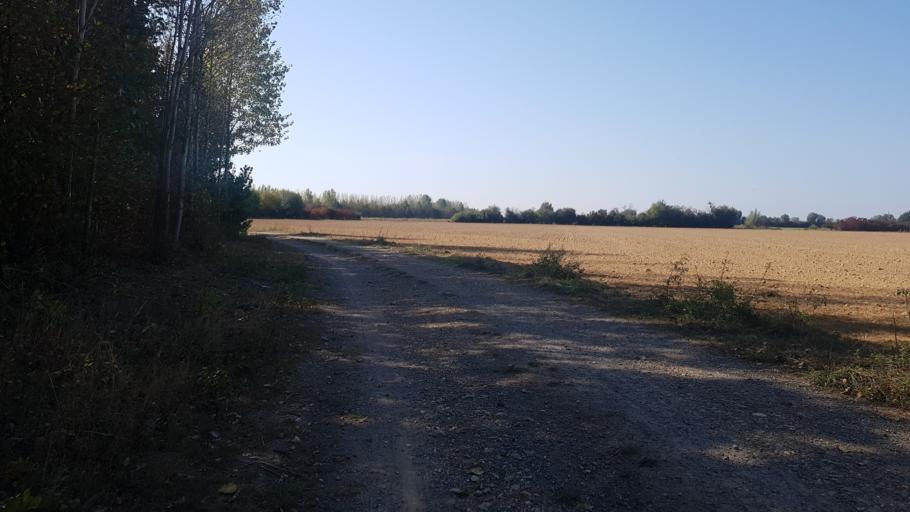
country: DE
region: North Rhine-Westphalia
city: Niedermerz
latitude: 50.8579
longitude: 6.2667
